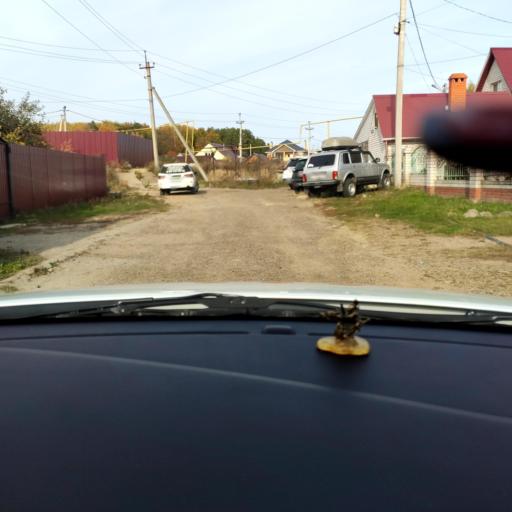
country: RU
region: Tatarstan
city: Vysokaya Gora
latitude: 55.9150
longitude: 49.2948
